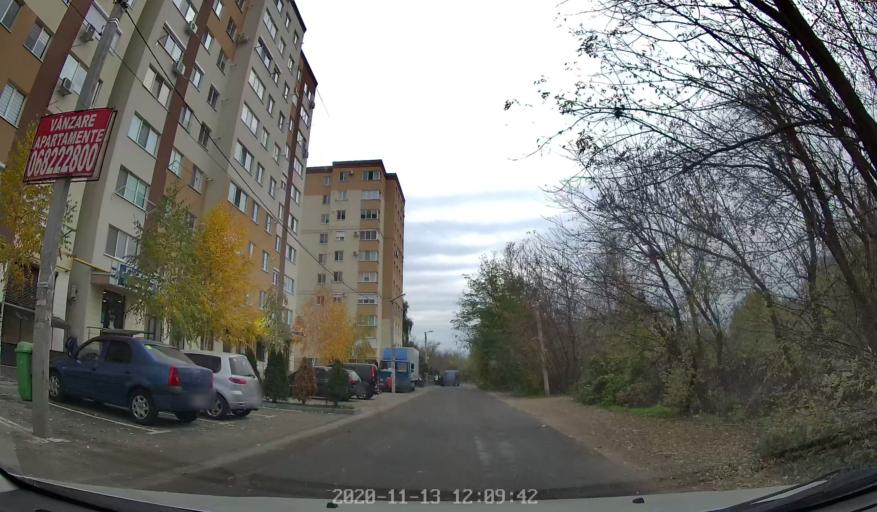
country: MD
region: Chisinau
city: Chisinau
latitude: 46.9577
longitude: 28.8369
